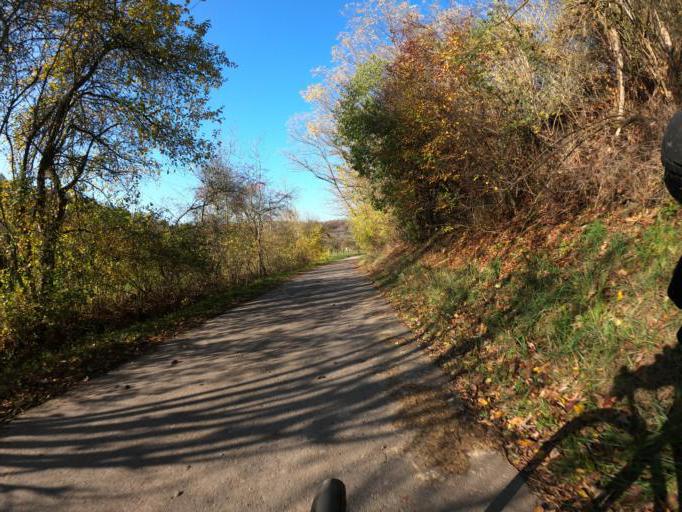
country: DE
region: Baden-Wuerttemberg
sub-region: Regierungsbezirk Stuttgart
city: Weil der Stadt
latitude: 48.7418
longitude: 8.8830
